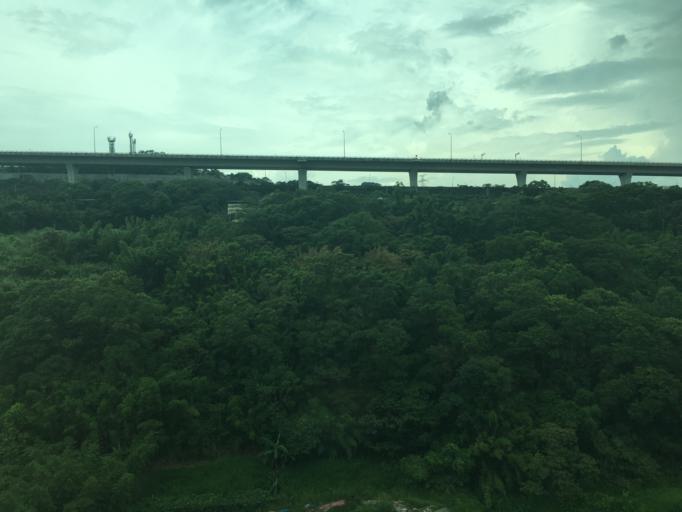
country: TW
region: Taiwan
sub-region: Taoyuan
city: Taoyuan
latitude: 25.0659
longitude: 121.3368
